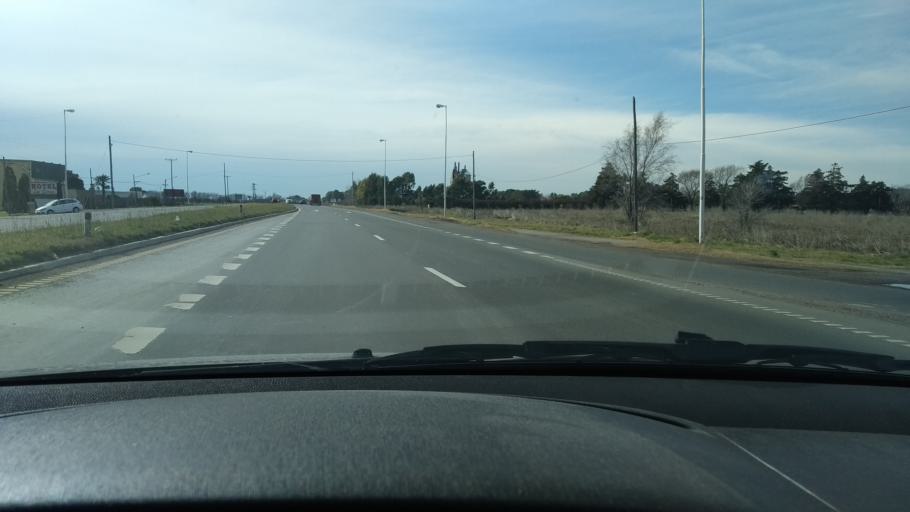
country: AR
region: Buenos Aires
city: Olavarria
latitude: -36.9162
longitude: -60.2042
